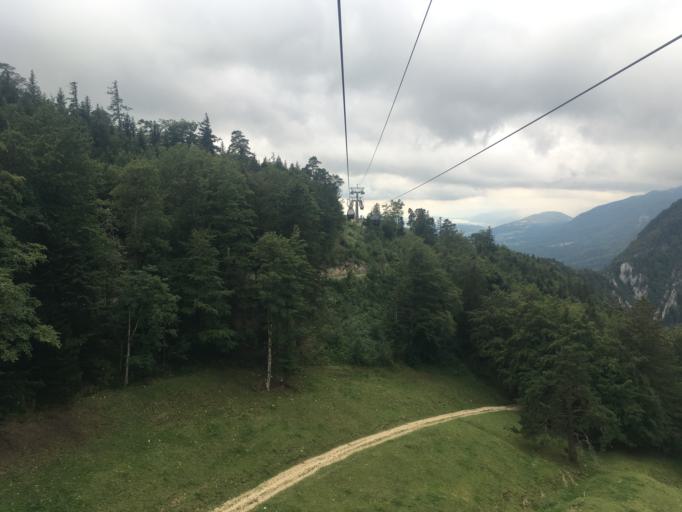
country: CH
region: Solothurn
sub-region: Bezirk Lebern
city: Langendorf
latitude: 47.2448
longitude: 7.5069
